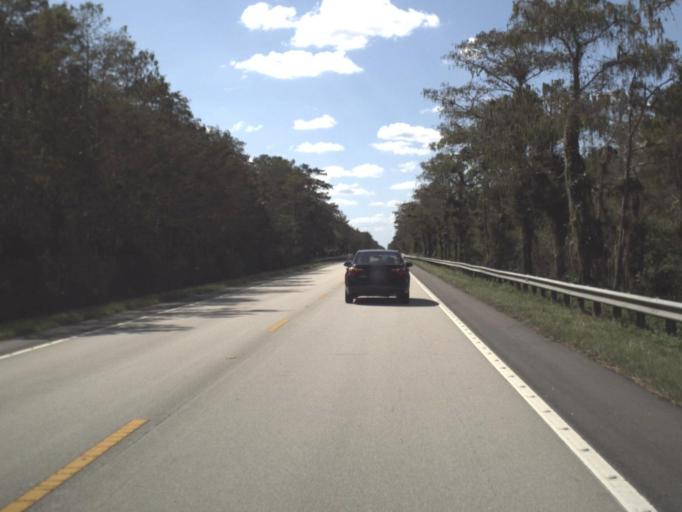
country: US
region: Florida
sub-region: Miami-Dade County
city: Kendall West
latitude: 25.8507
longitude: -80.9722
